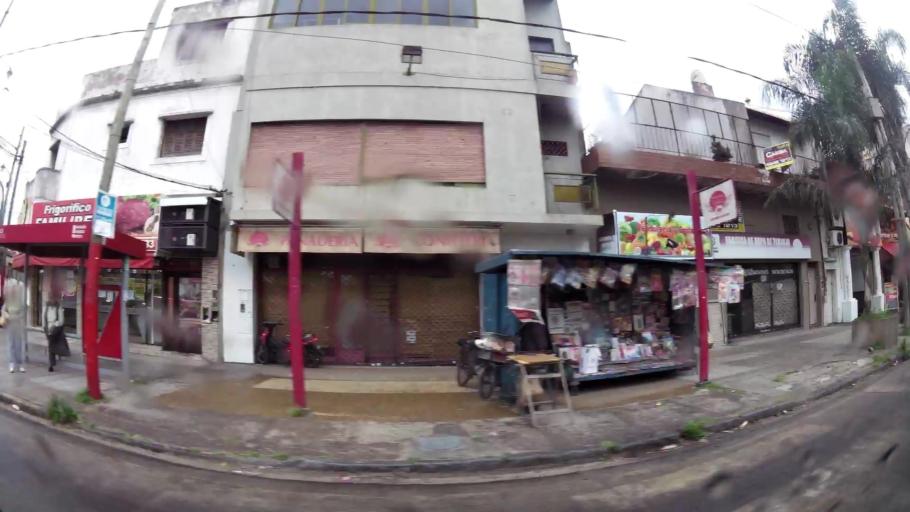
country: AR
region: Buenos Aires
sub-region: Partido de Lanus
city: Lanus
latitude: -34.6858
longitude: -58.4050
